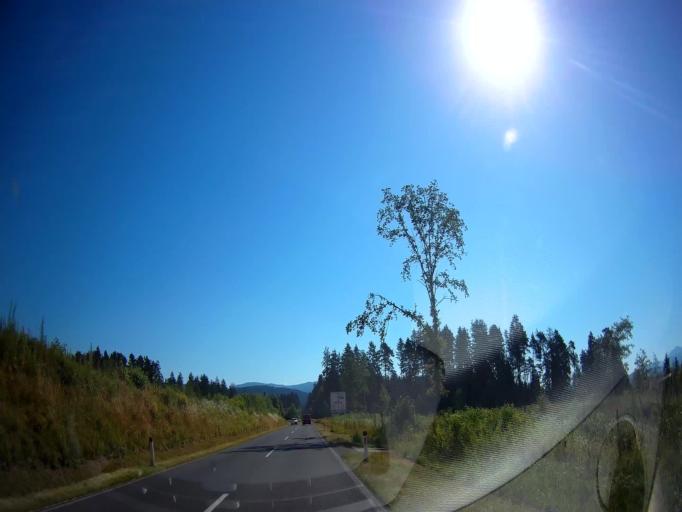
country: AT
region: Carinthia
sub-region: Politischer Bezirk Volkermarkt
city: Feistritz ob Bleiburg
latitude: 46.5745
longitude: 14.7503
